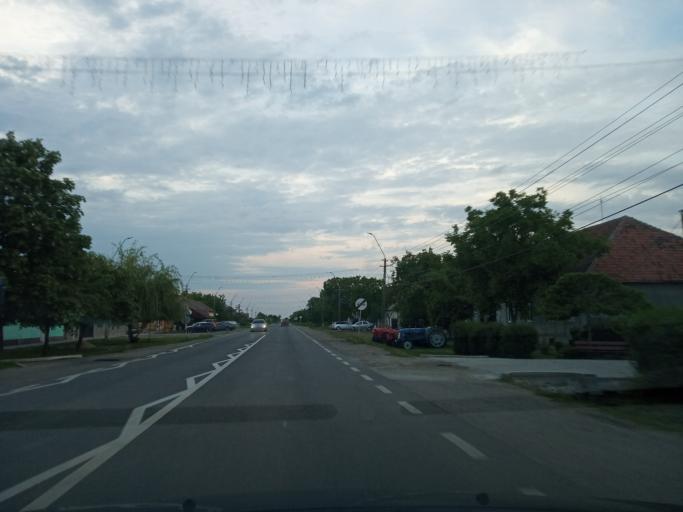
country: RO
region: Timis
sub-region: Comuna Voiteg
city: Voiteg
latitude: 45.4709
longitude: 21.2346
